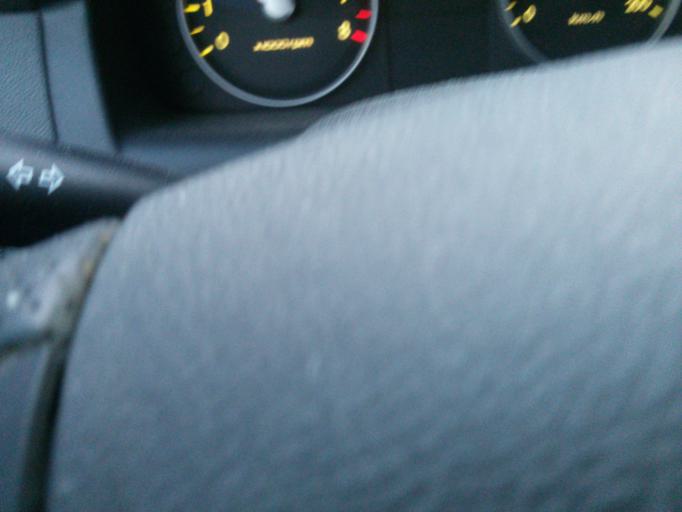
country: IT
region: Liguria
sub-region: Provincia di Genova
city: Genoa
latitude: 44.4541
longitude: 8.8942
